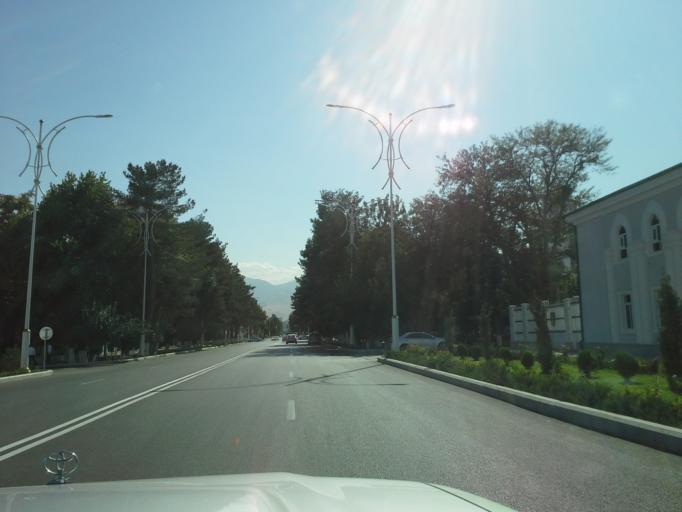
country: TM
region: Ahal
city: Ashgabat
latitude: 37.9423
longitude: 58.3952
